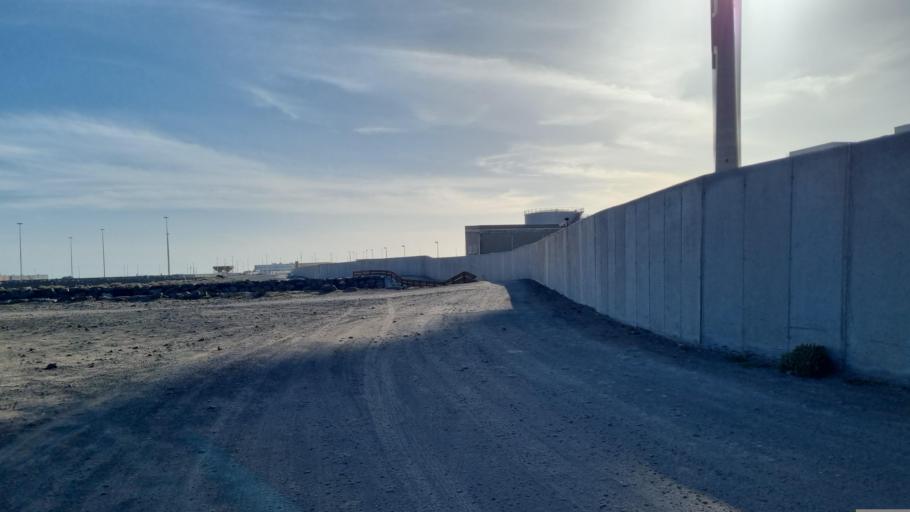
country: ES
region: Canary Islands
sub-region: Provincia de Santa Cruz de Tenerife
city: San Isidro
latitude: 28.0861
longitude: -16.4901
